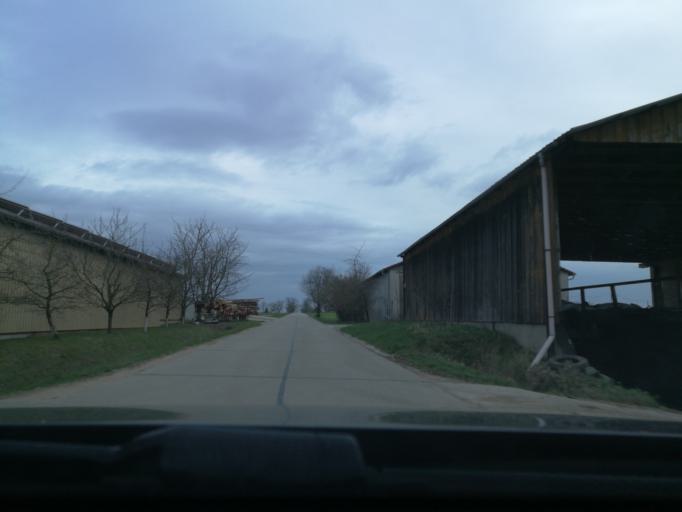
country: DE
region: Bavaria
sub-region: Regierungsbezirk Mittelfranken
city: Obermichelbach
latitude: 49.5299
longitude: 10.9579
